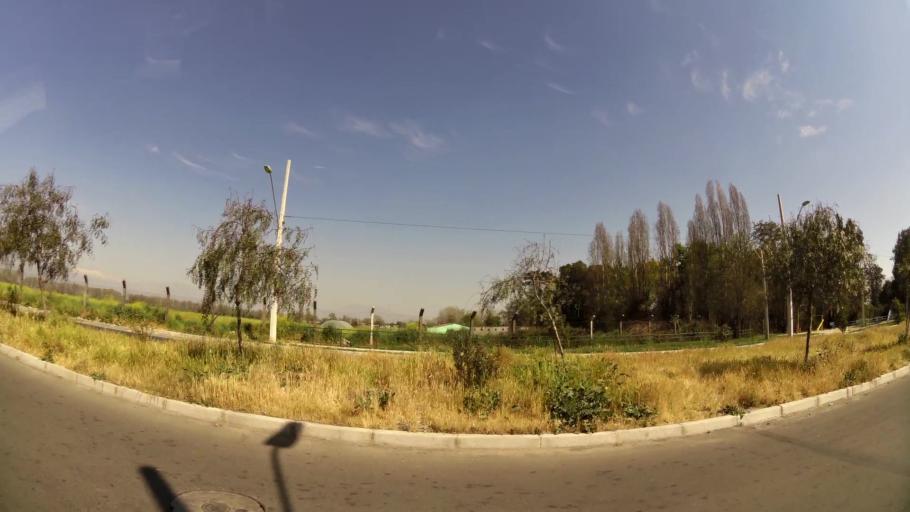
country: CL
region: Santiago Metropolitan
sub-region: Provincia de Santiago
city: La Pintana
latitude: -33.5660
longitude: -70.6277
